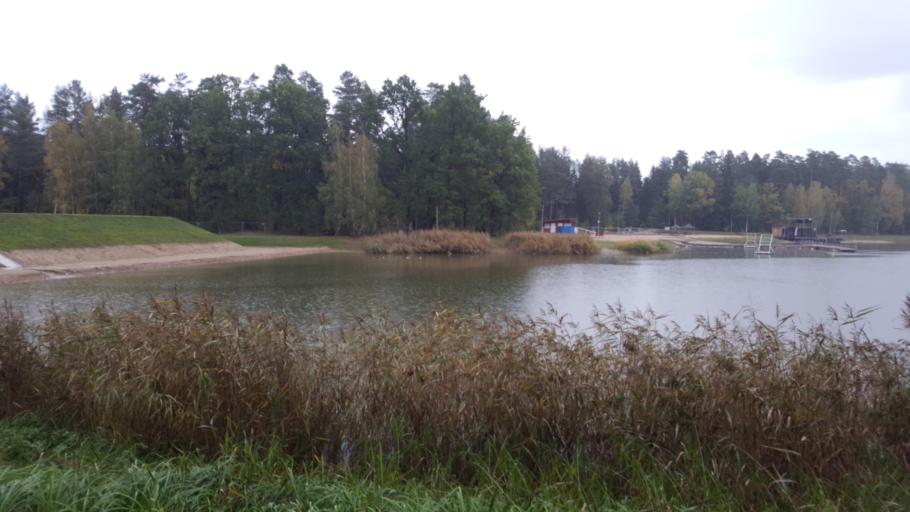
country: LT
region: Alytaus apskritis
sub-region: Alytus
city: Alytus
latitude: 54.3866
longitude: 24.0663
